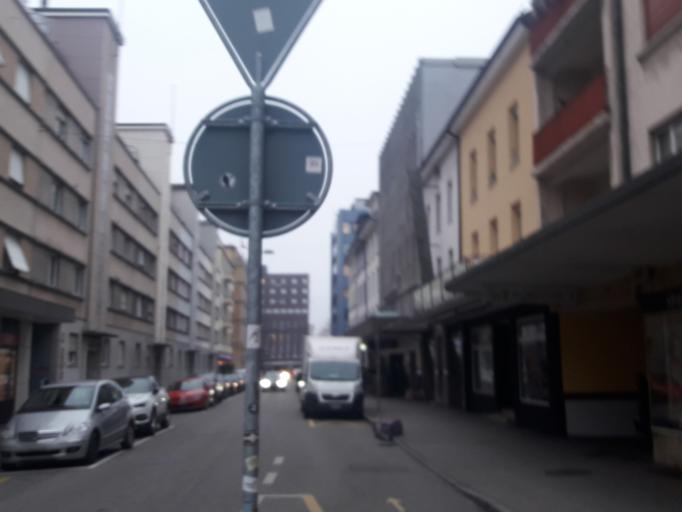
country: CH
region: Bern
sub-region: Biel/Bienne District
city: Biel/Bienne
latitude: 47.1350
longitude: 7.2465
